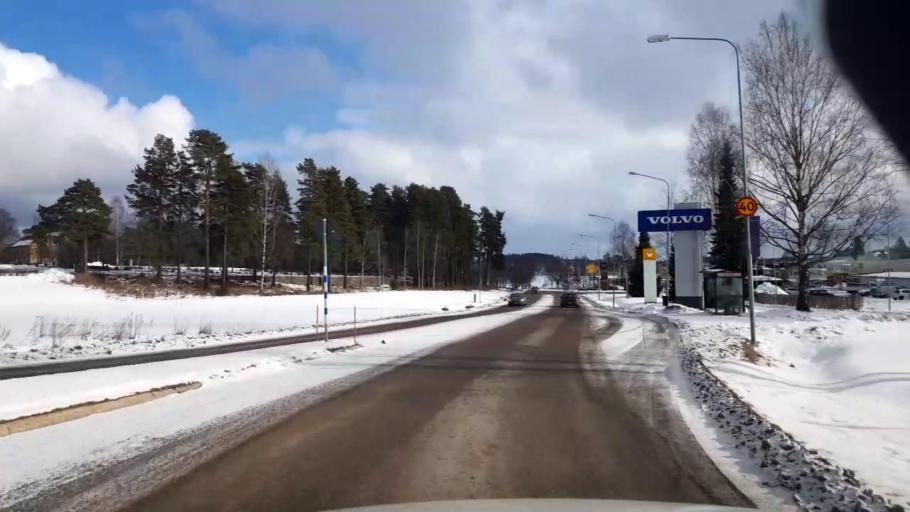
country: SE
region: Gaevleborg
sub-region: Hudiksvalls Kommun
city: Hudiksvall
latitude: 61.7353
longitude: 17.0954
